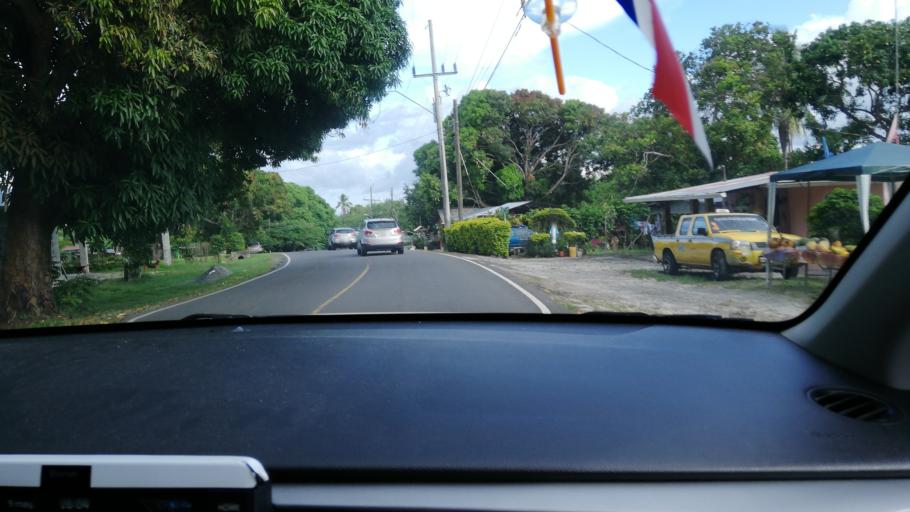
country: PA
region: Panama
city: Las Colinas
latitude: 8.5227
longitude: -80.0377
